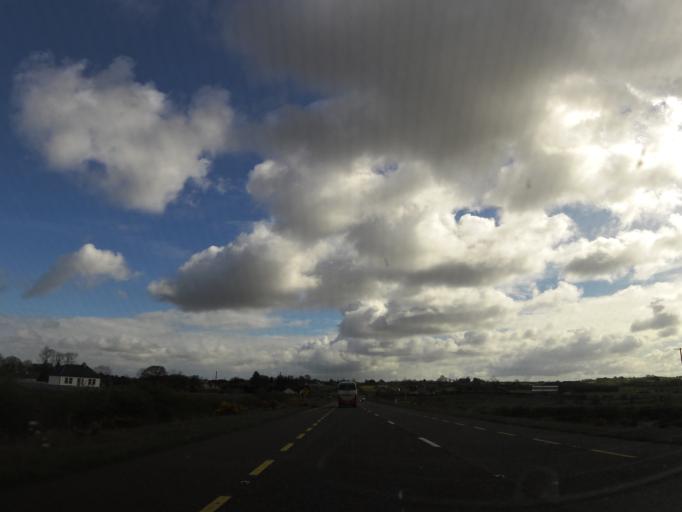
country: IE
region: Connaught
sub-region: Maigh Eo
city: Kiltamagh
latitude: 53.8253
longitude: -8.8808
